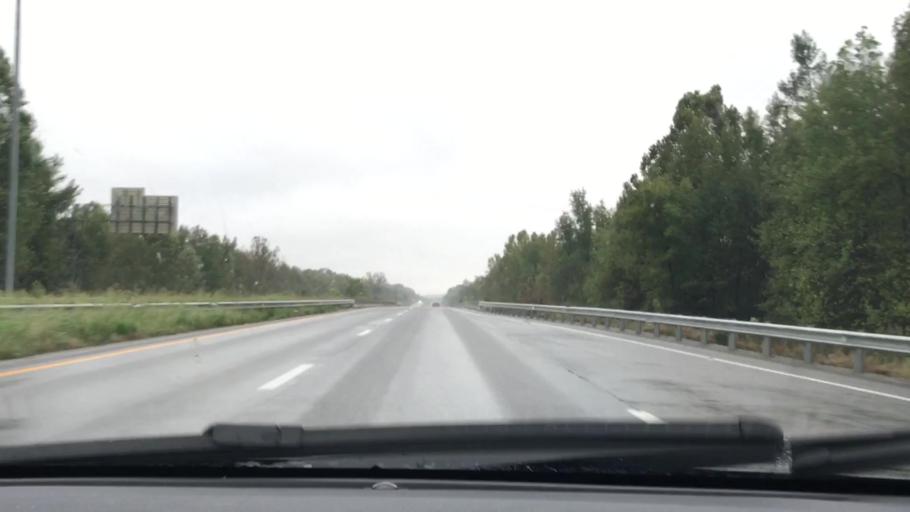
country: US
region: Kentucky
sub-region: Hopkins County
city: Nortonville
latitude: 37.1900
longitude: -87.4428
